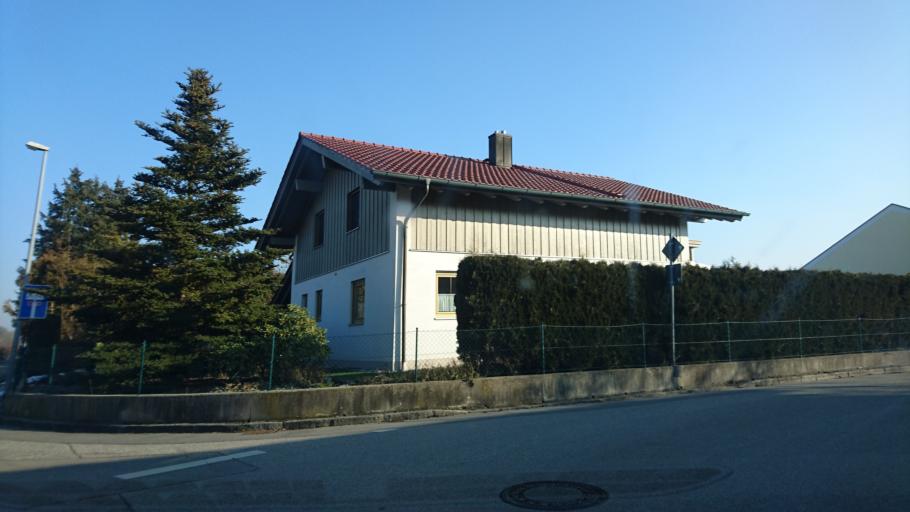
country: DE
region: Bavaria
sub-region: Lower Bavaria
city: Pfarrkirchen
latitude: 48.4297
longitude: 12.9444
